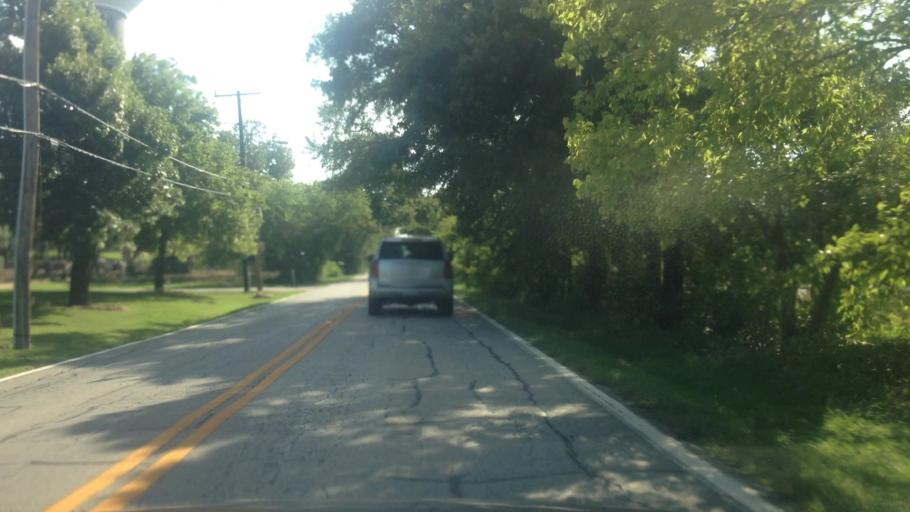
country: US
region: Texas
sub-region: Tarrant County
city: Colleyville
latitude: 32.8743
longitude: -97.1951
